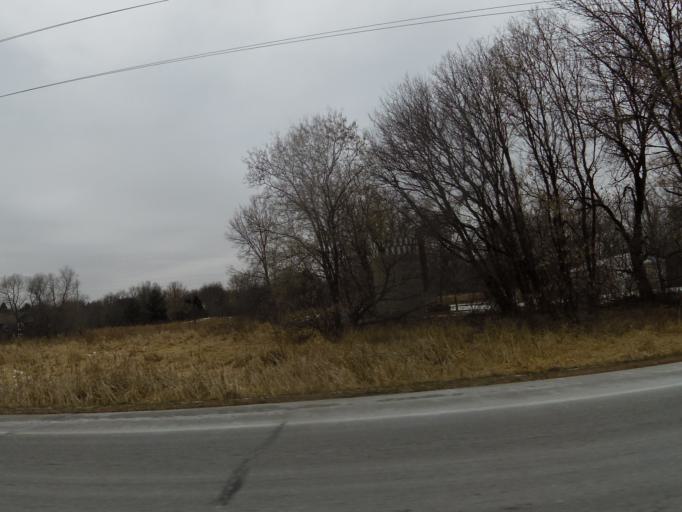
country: US
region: Minnesota
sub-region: Hennepin County
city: Long Lake
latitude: 44.9986
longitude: -93.5854
